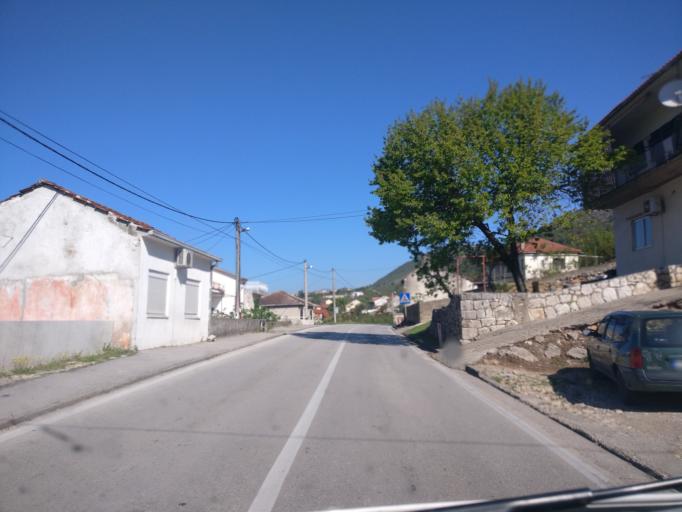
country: BA
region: Federation of Bosnia and Herzegovina
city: Capljina
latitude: 43.1369
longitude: 17.6714
